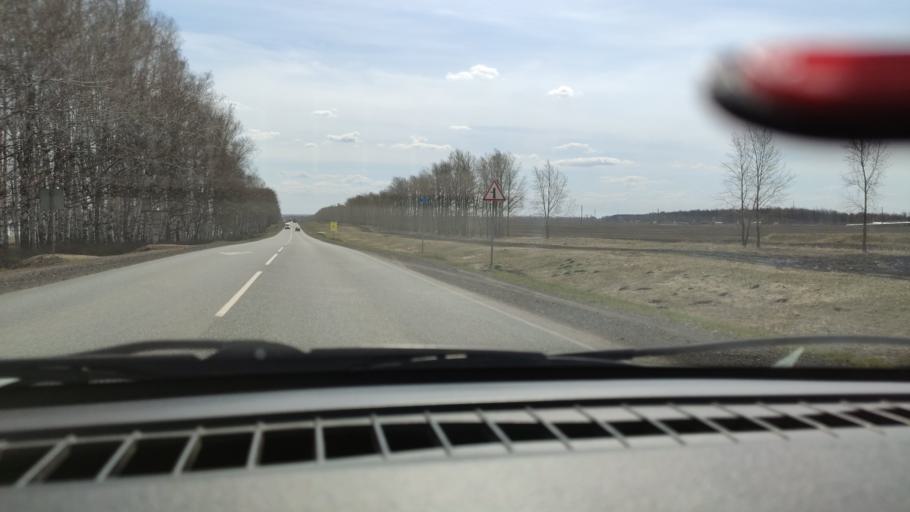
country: RU
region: Bashkortostan
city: Kushnarenkovo
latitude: 55.2184
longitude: 55.0944
